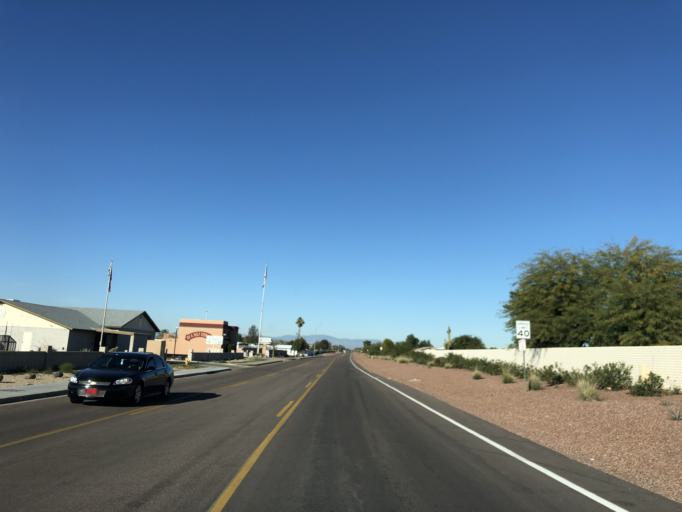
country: US
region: Arizona
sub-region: Maricopa County
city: Surprise
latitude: 33.6537
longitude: -112.2899
